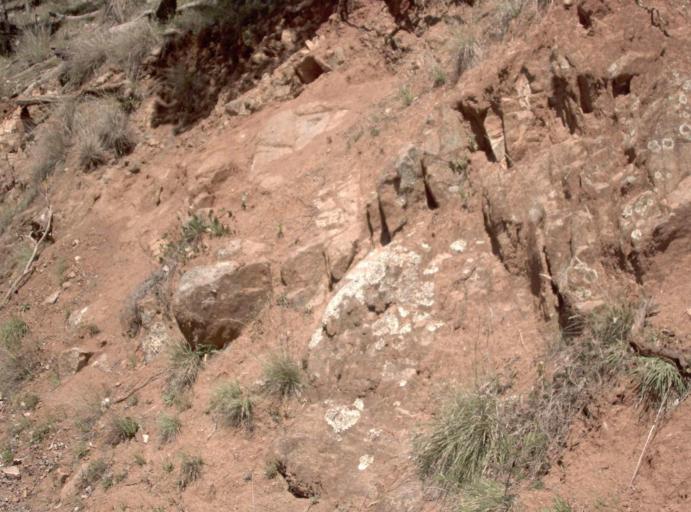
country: AU
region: New South Wales
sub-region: Snowy River
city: Jindabyne
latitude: -37.0604
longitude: 148.5253
